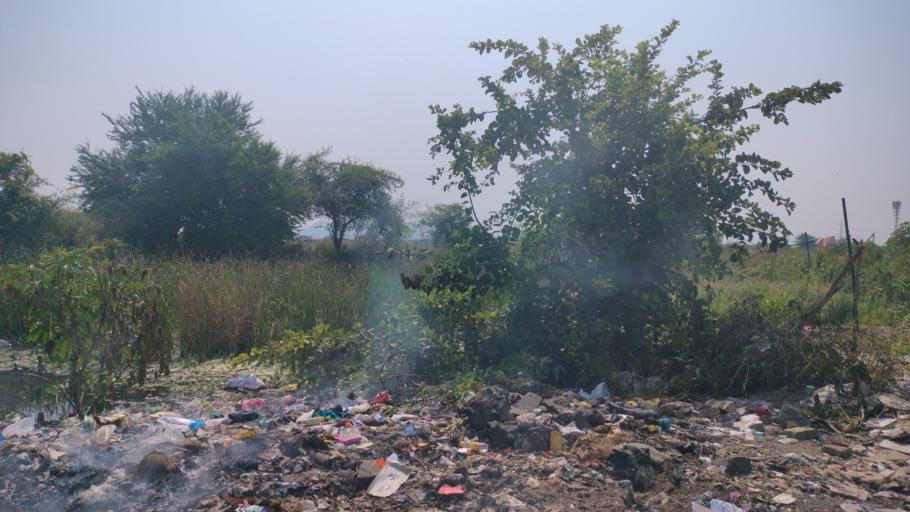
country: IN
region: Maharashtra
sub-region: Thane
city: Bhayandar
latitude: 19.3538
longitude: 72.8738
